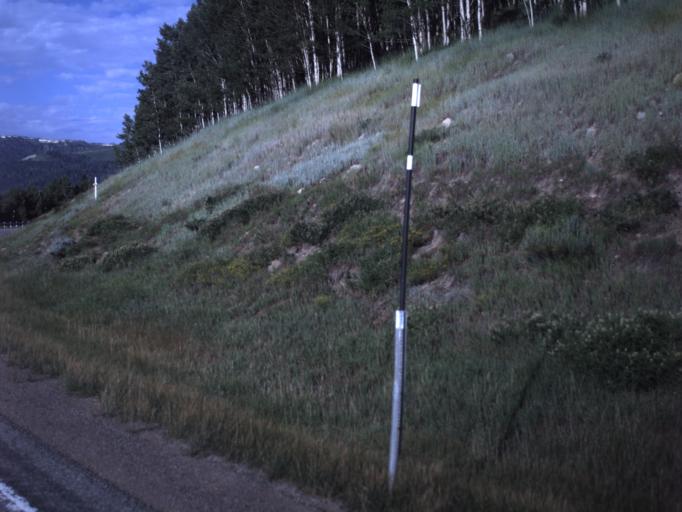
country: US
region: Utah
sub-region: Sanpete County
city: Fairview
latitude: 39.5836
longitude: -111.2297
